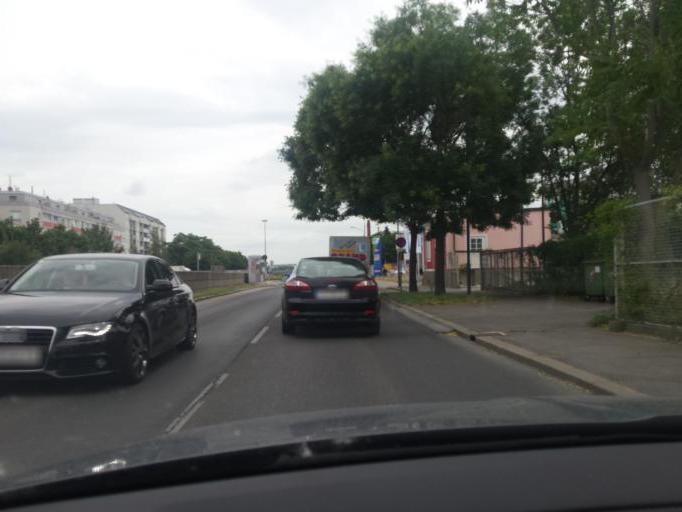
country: AT
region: Vienna
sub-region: Wien Stadt
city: Vienna
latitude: 48.1709
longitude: 16.4091
